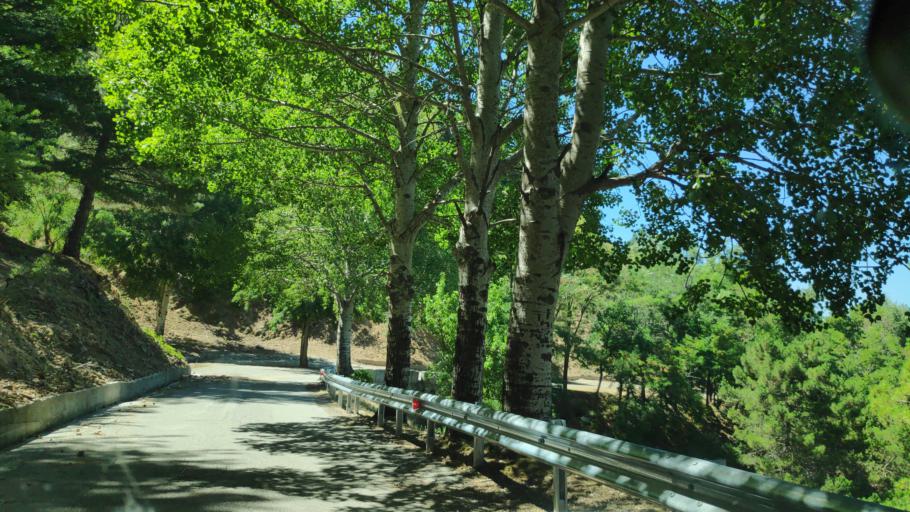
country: IT
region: Calabria
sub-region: Provincia di Reggio Calabria
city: Africo Vecchio
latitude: 38.0386
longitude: 15.9510
